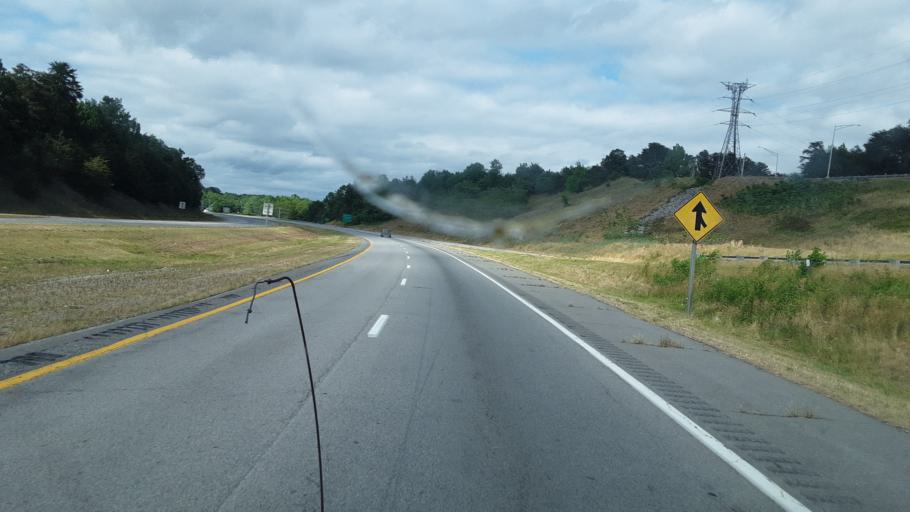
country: US
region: Virginia
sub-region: City of Danville
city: Danville
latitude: 36.5748
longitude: -79.3645
